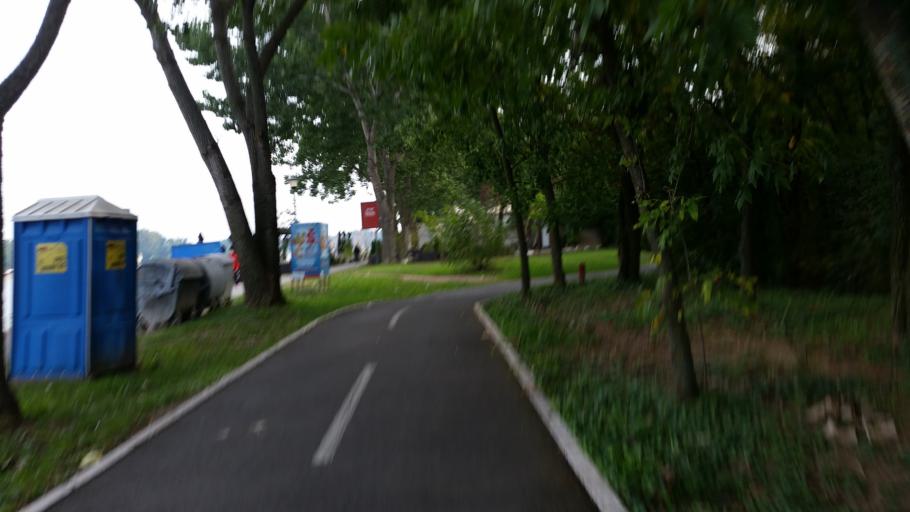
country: RS
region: Central Serbia
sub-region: Belgrade
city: Cukarica
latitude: 44.7794
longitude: 20.3818
